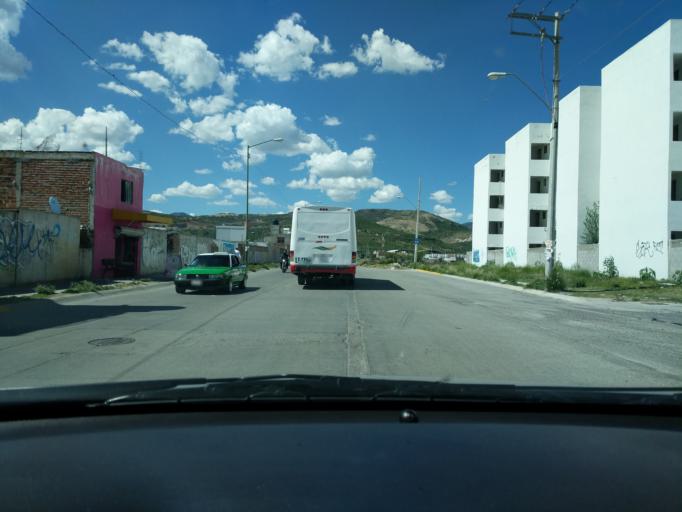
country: MX
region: Guanajuato
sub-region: Leon
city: Fraccionamiento Paraiso Real
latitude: 21.1011
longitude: -101.5785
